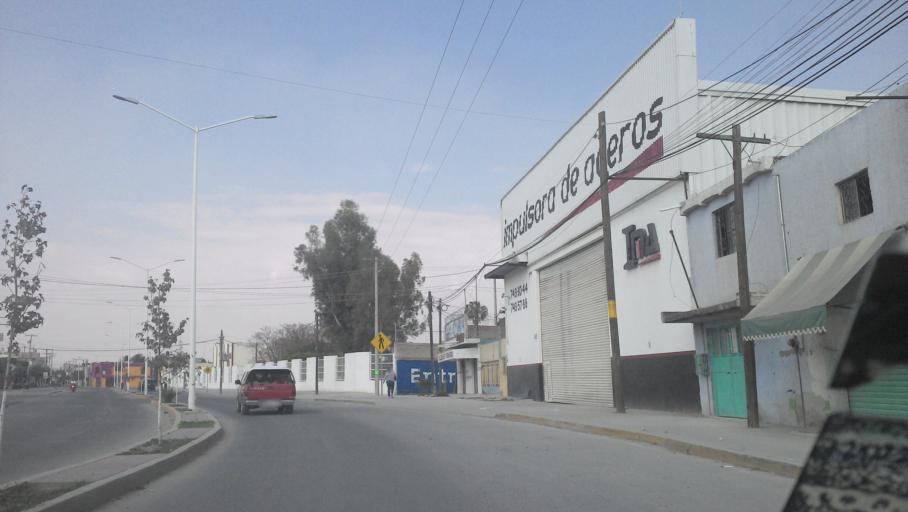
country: MX
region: Guanajuato
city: San Francisco del Rincon
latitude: 21.0083
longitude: -101.8514
